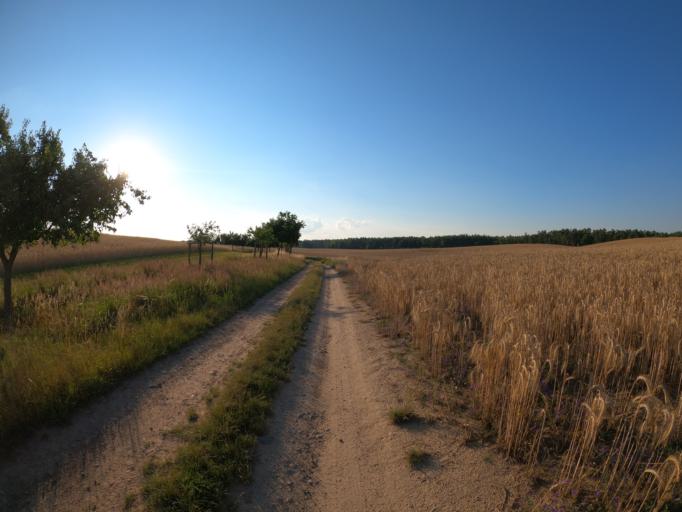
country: DE
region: Brandenburg
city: Althuttendorf
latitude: 53.0340
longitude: 13.8748
